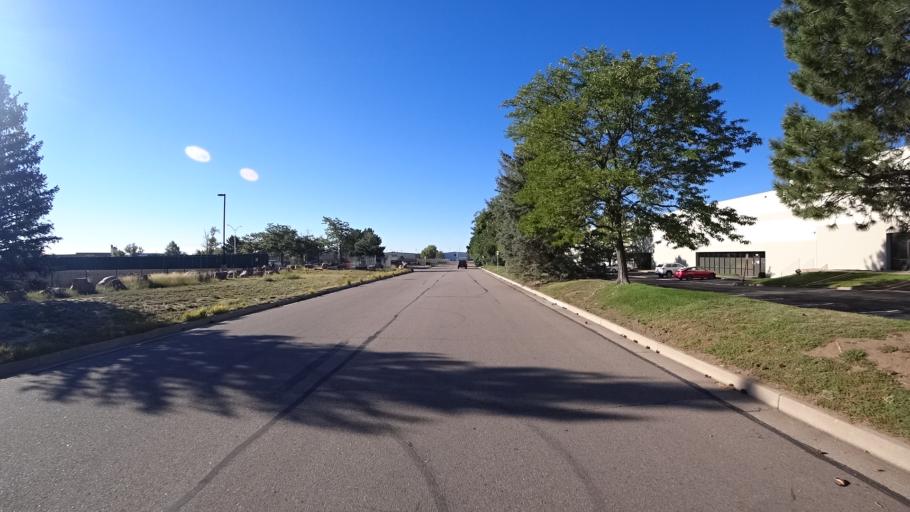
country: US
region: Colorado
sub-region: El Paso County
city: Security-Widefield
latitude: 38.7951
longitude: -104.7238
